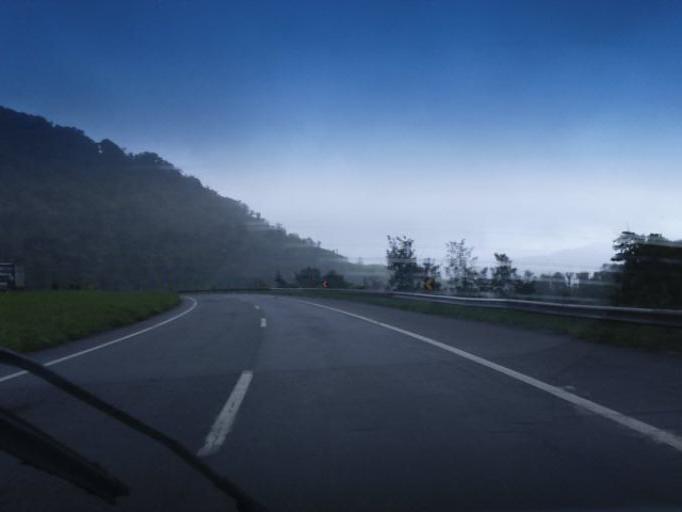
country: BR
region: Parana
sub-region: Antonina
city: Antonina
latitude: -25.0280
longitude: -48.5259
